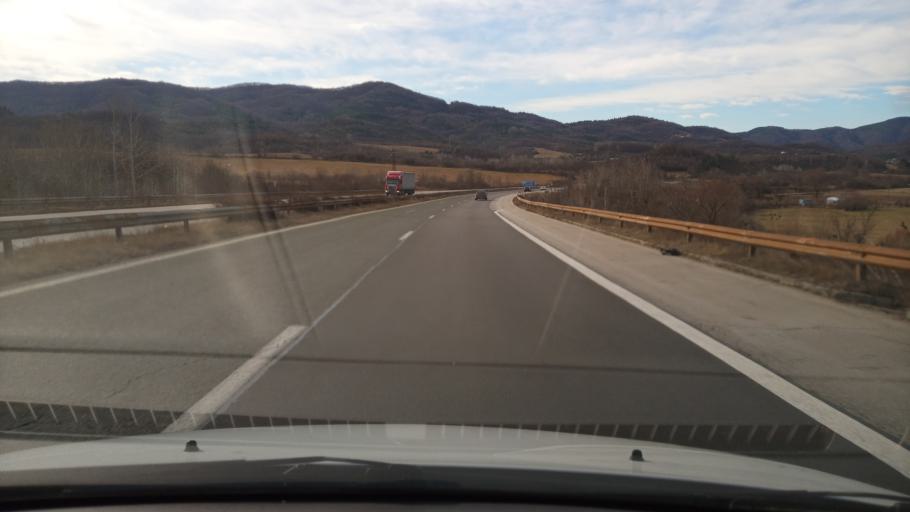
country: BG
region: Sofiya
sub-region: Obshtina Pravets
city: Pravets
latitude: 42.9381
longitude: 23.9710
